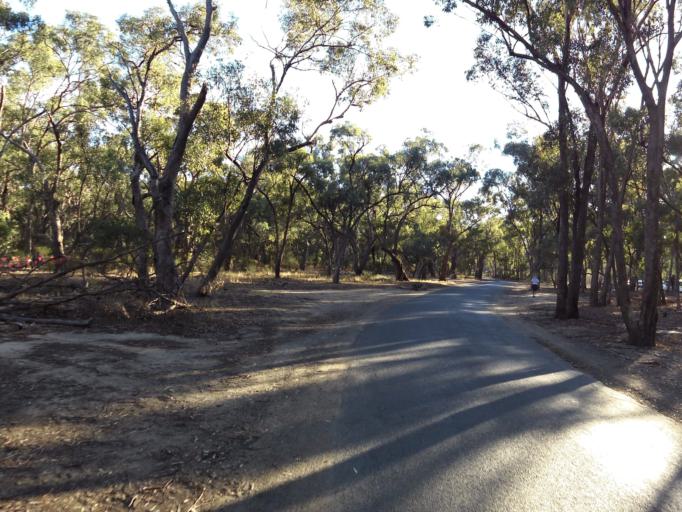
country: AU
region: New South Wales
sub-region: Murray Shire
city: Moama
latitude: -36.1127
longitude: 144.7414
